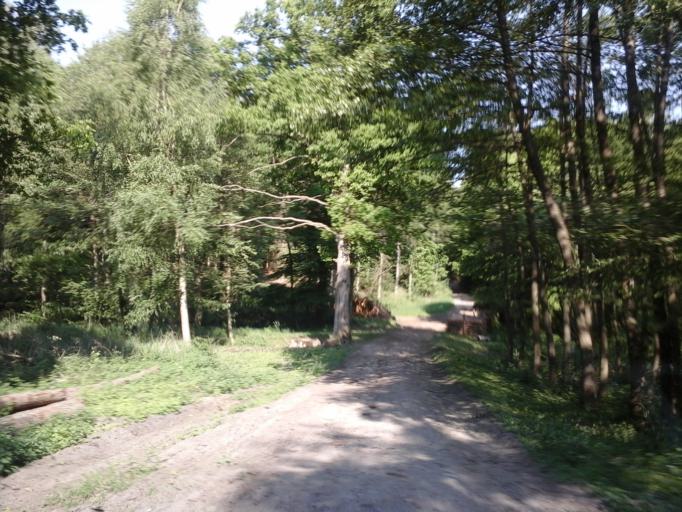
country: PL
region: West Pomeranian Voivodeship
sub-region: Powiat choszczenski
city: Recz
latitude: 53.3268
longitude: 15.5297
